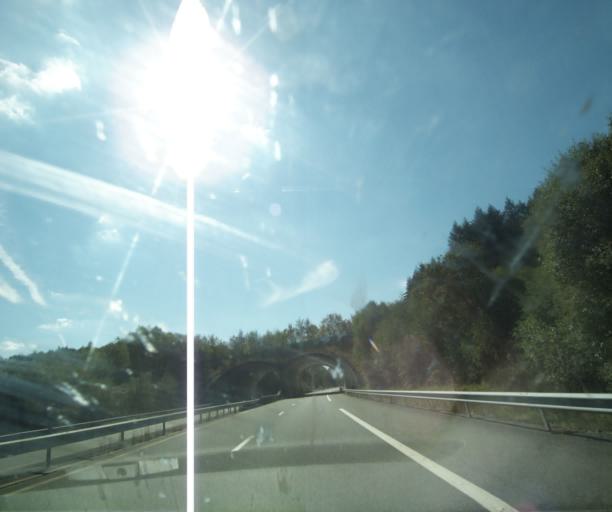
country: FR
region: Limousin
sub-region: Departement de la Correze
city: Egletons
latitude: 45.3744
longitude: 1.9660
